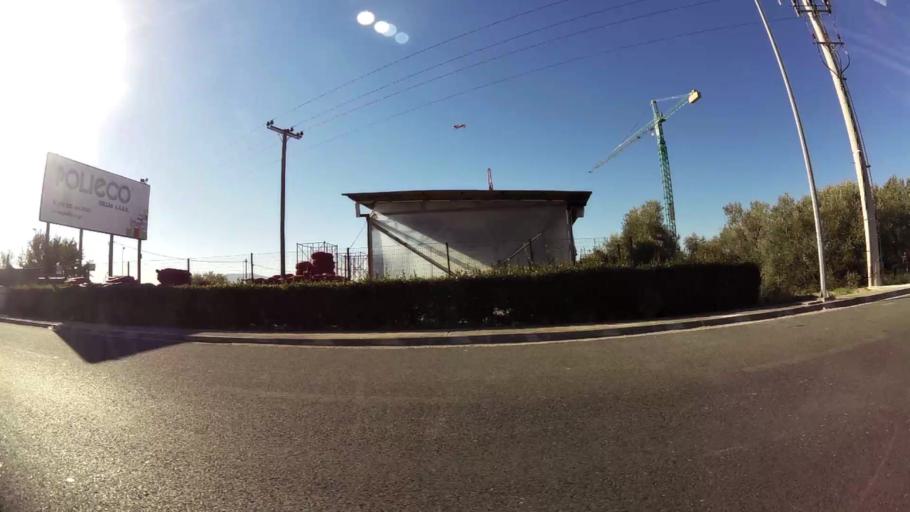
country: GR
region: Attica
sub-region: Nomarchia Athinas
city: Metamorfosi
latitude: 38.0967
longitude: 23.7717
